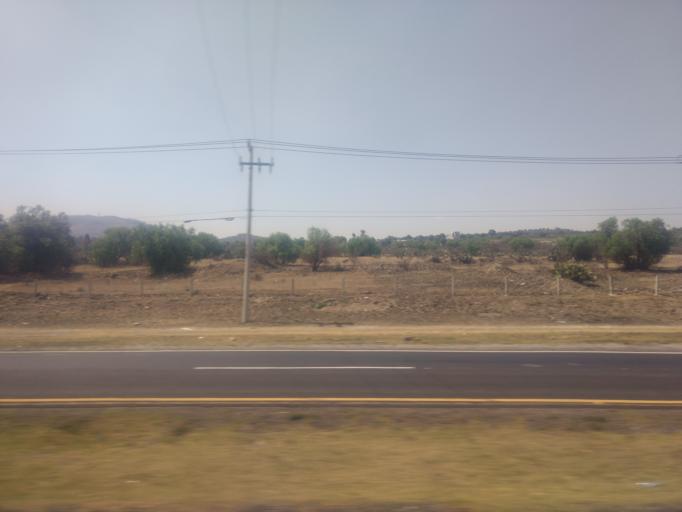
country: MX
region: Morelos
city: Axapusco
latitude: 19.7392
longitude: -98.7687
